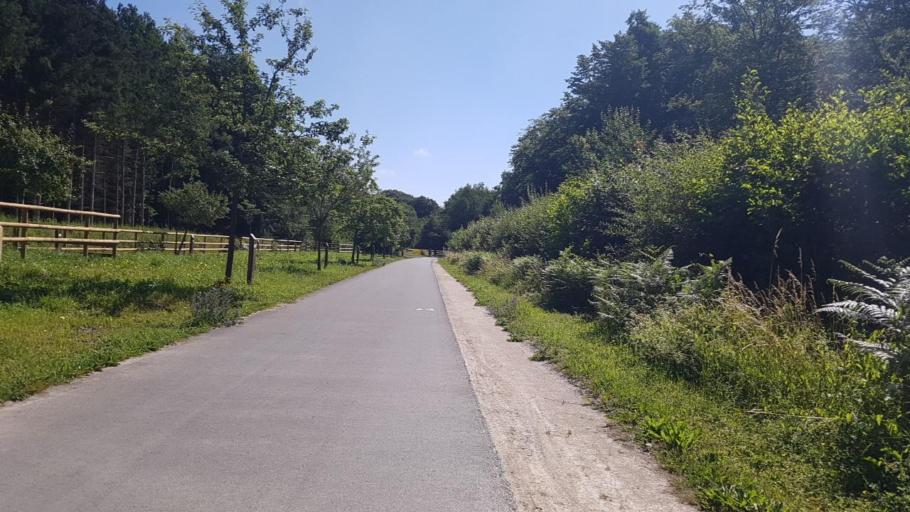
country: BE
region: Wallonia
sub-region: Province du Hainaut
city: Momignies
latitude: 50.0273
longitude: 4.1852
